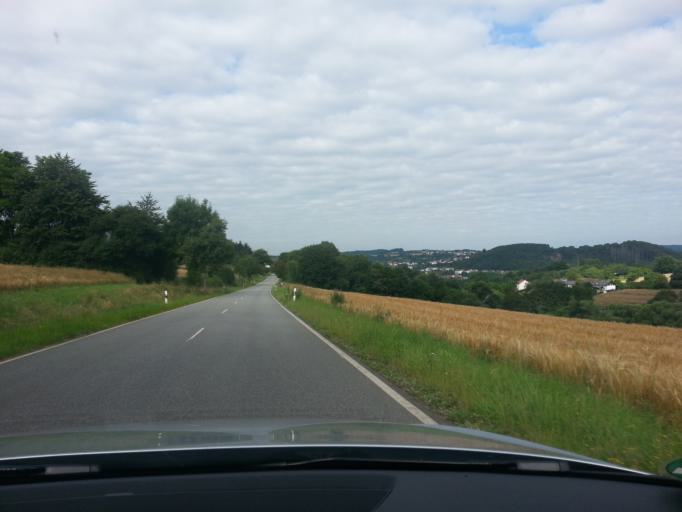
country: DE
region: Saarland
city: Schmelz
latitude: 49.4459
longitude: 6.8719
